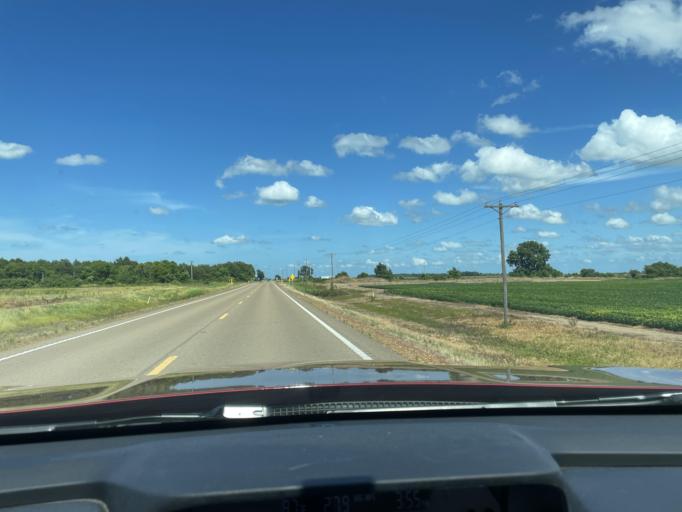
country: US
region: Mississippi
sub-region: Humphreys County
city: Belzoni
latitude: 33.1826
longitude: -90.6358
